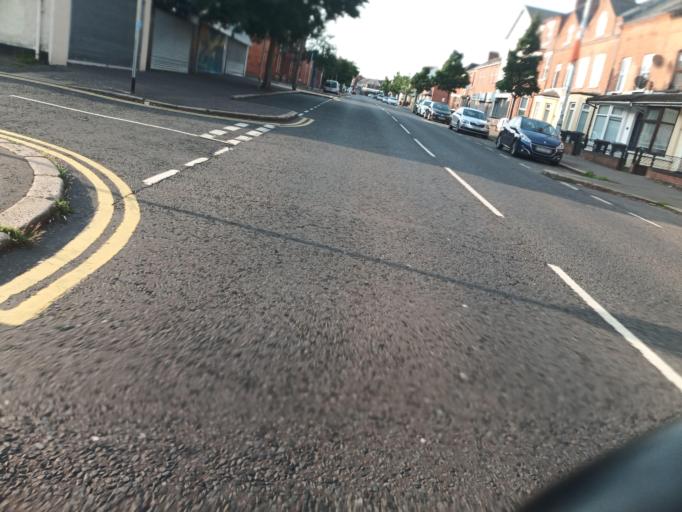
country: GB
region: Northern Ireland
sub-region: Castlereagh District
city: Castlereagh
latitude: 54.5958
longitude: -5.8884
